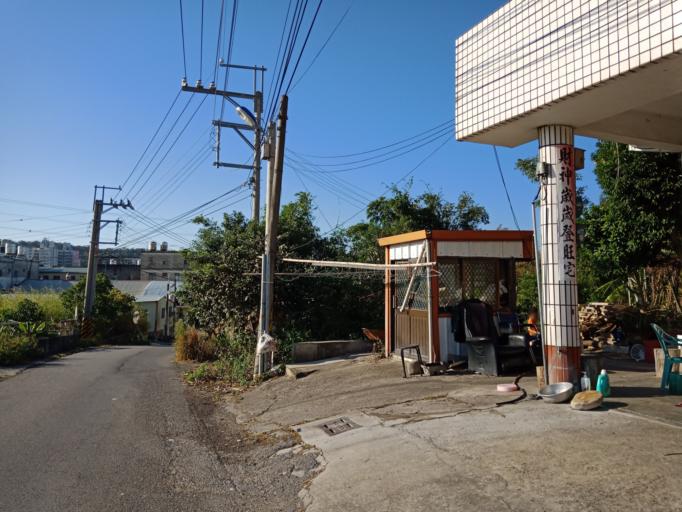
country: TW
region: Taiwan
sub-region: Miaoli
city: Miaoli
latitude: 24.4928
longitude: 120.6945
